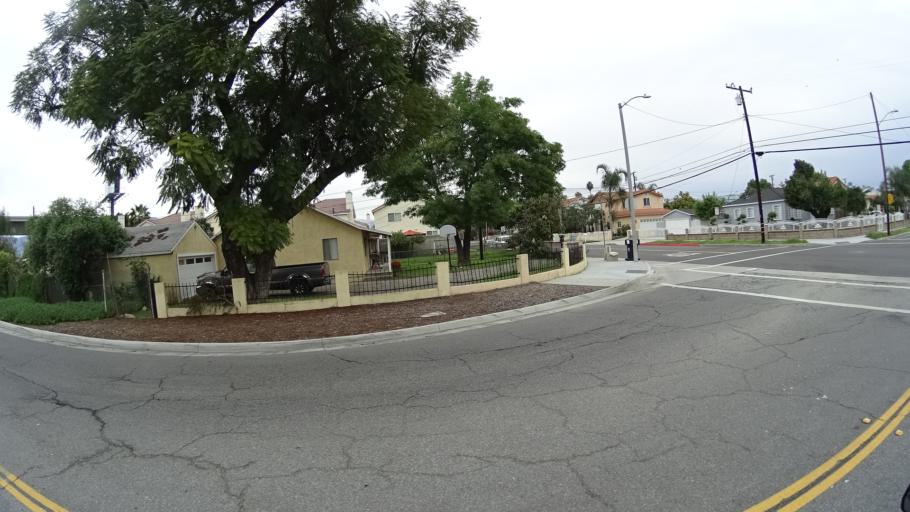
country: US
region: California
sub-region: Los Angeles County
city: West Puente Valley
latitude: 34.0647
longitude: -117.9930
